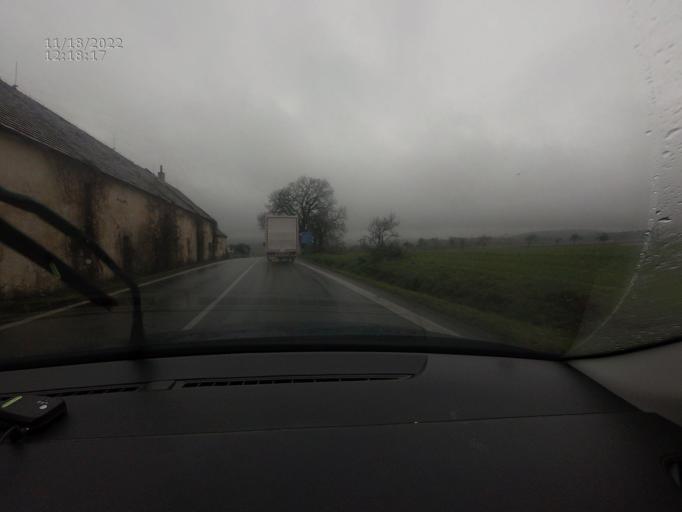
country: CZ
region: Plzensky
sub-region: Okres Plzen-Jih
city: Nepomuk
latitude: 49.4870
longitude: 13.5665
